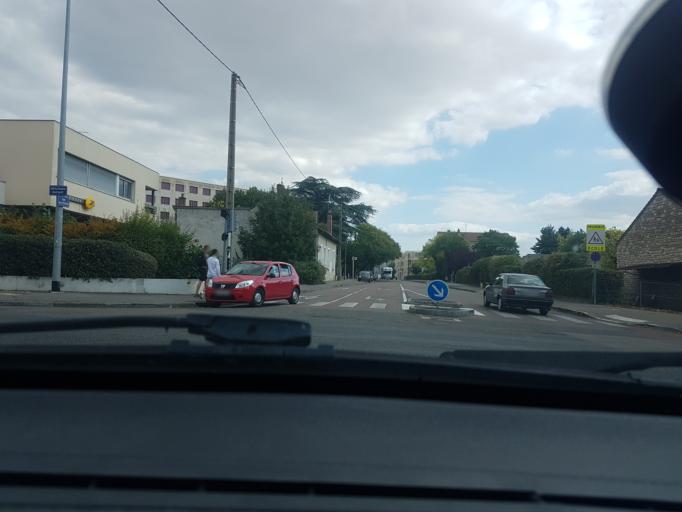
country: FR
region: Bourgogne
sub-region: Departement de la Cote-d'Or
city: Longvic
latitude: 47.3104
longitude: 5.0598
